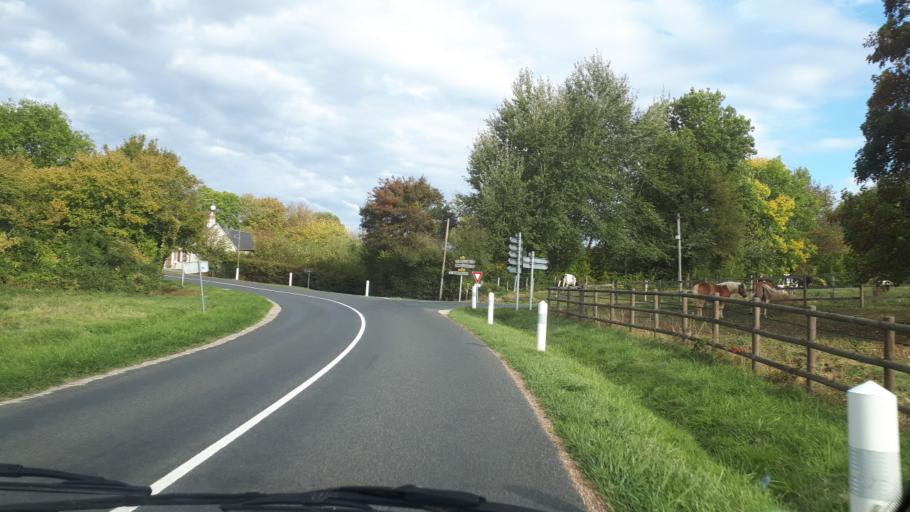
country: FR
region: Centre
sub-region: Departement du Loir-et-Cher
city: Mondoubleau
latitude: 47.9755
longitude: 0.9128
